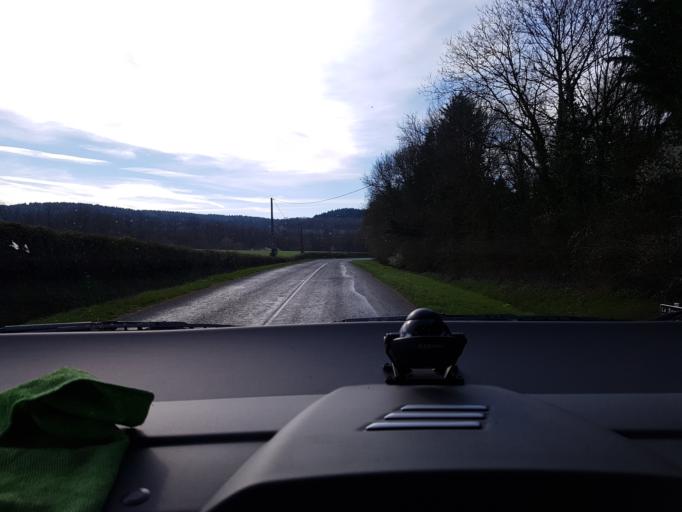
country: FR
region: Bourgogne
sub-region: Departement de Saone-et-Loire
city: Toulon-sur-Arroux
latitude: 46.7346
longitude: 4.1281
